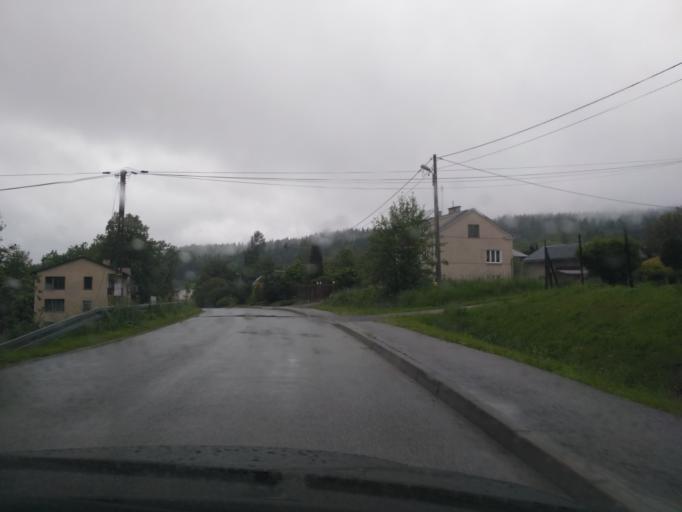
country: PL
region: Lesser Poland Voivodeship
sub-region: Powiat gorlicki
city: Sekowa
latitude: 49.6204
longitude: 21.2285
